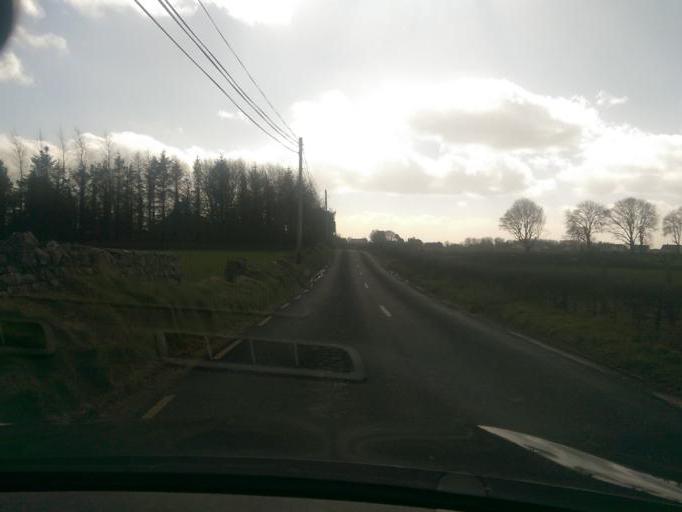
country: IE
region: Connaught
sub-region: County Galway
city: Athenry
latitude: 53.3557
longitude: -8.7054
